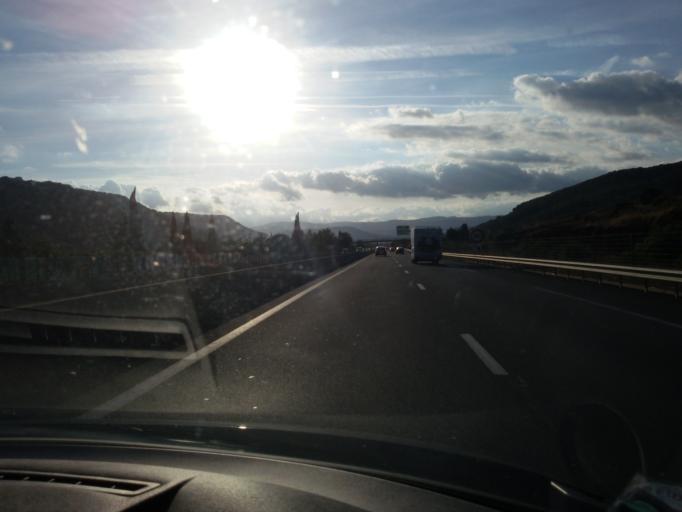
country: FR
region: Languedoc-Roussillon
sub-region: Departement de l'Herault
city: Nebian
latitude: 43.6773
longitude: 3.4121
